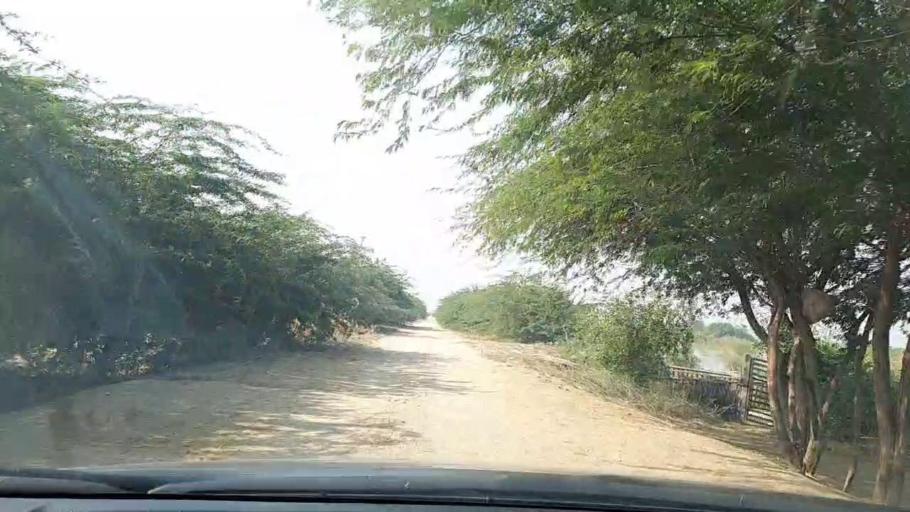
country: PK
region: Sindh
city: Mirpur Sakro
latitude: 24.5749
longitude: 67.7731
